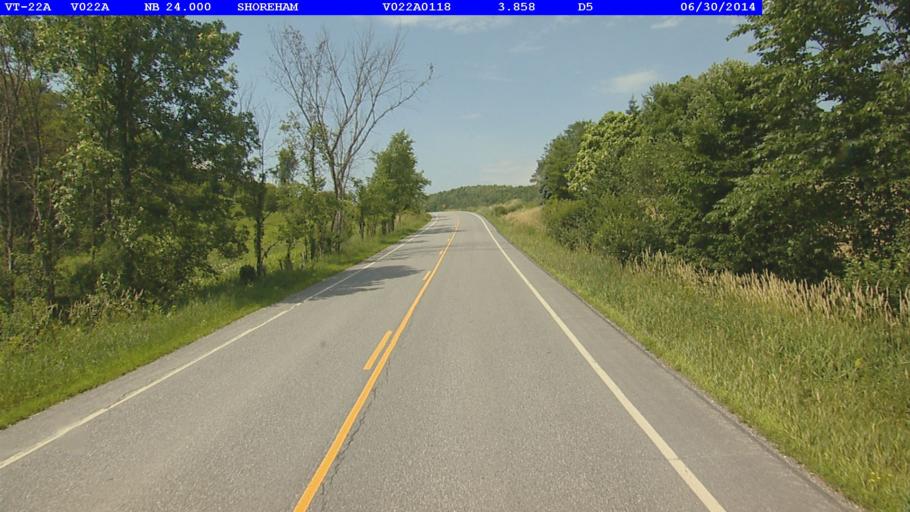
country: US
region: New York
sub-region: Essex County
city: Ticonderoga
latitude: 43.9052
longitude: -73.3083
